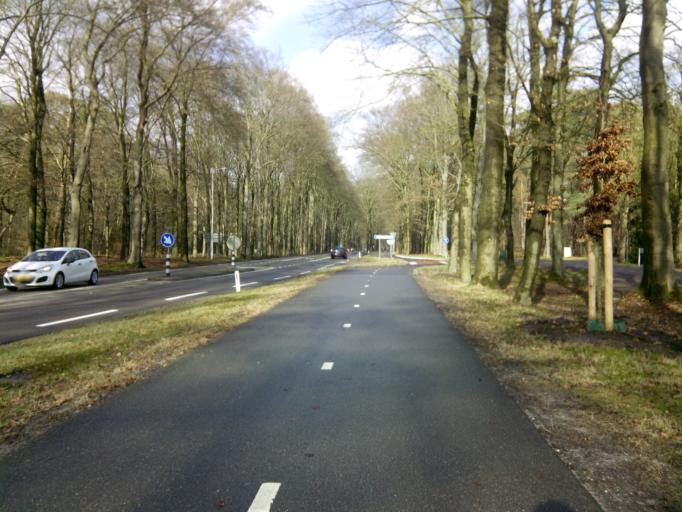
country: NL
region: Utrecht
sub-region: Gemeente Utrechtse Heuvelrug
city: Maarsbergen
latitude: 52.0408
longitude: 5.4113
